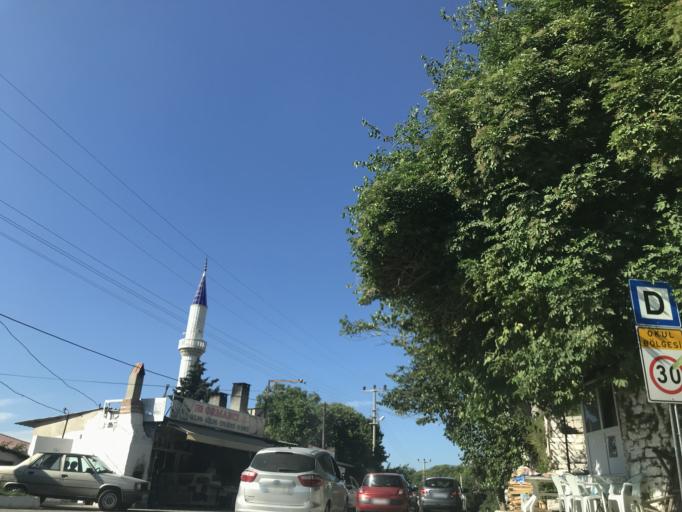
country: TR
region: Aydin
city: Davutlar
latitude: 37.7382
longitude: 27.3412
